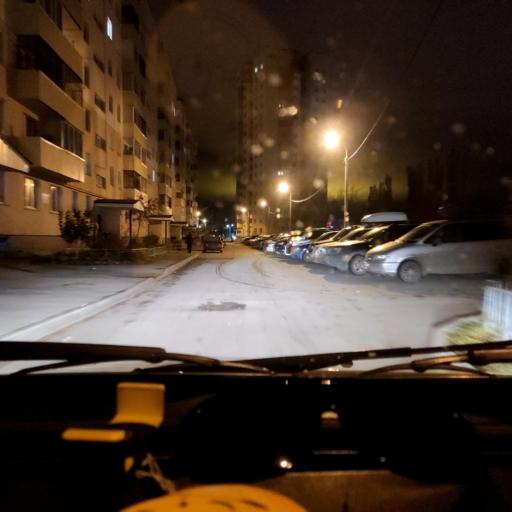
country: RU
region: Bashkortostan
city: Ufa
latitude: 54.7703
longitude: 56.0661
